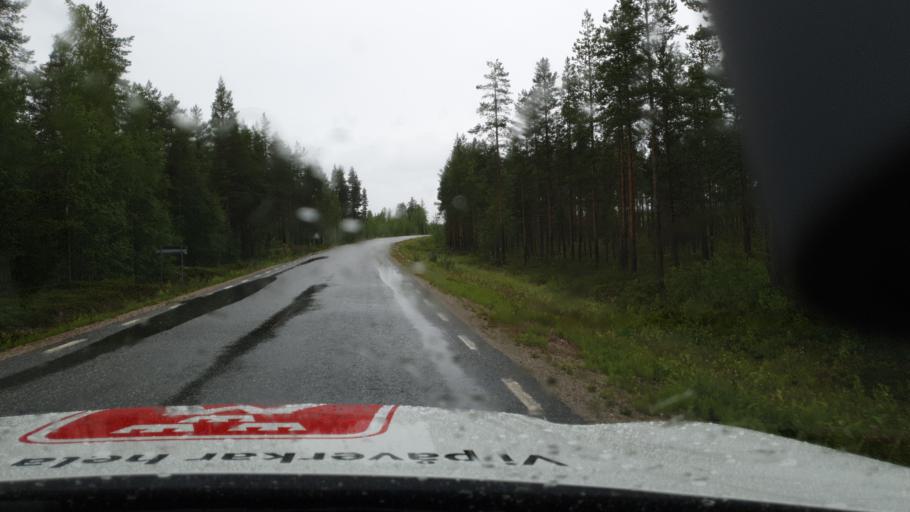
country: SE
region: Vaesterbotten
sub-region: Vindelns Kommun
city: Vindeln
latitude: 64.5019
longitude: 19.7981
